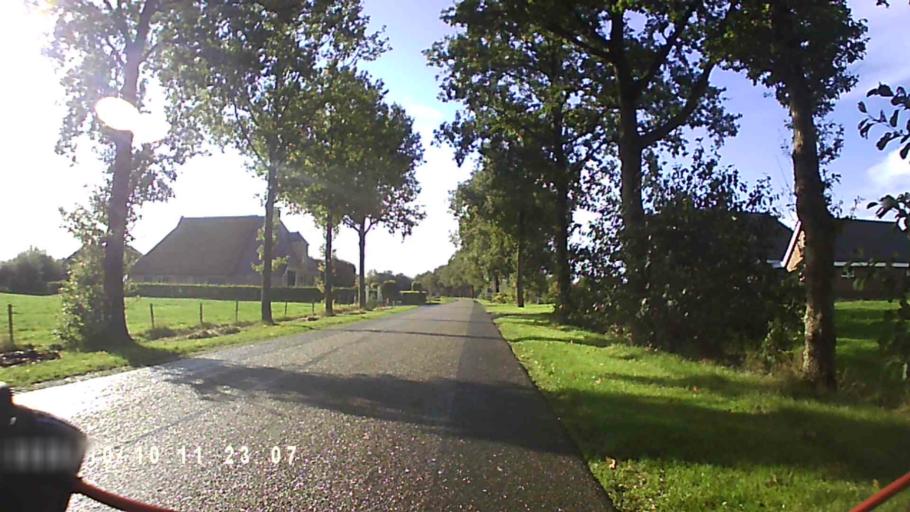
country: NL
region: Friesland
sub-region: Gemeente Smallingerland
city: Drachtstercompagnie
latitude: 53.0911
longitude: 6.1772
